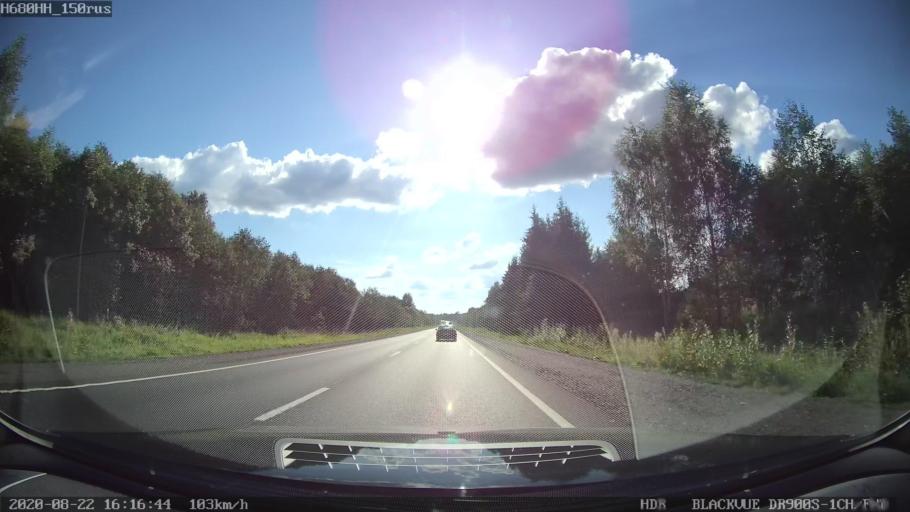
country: RU
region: Tverskaya
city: Rameshki
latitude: 57.4315
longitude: 36.1731
